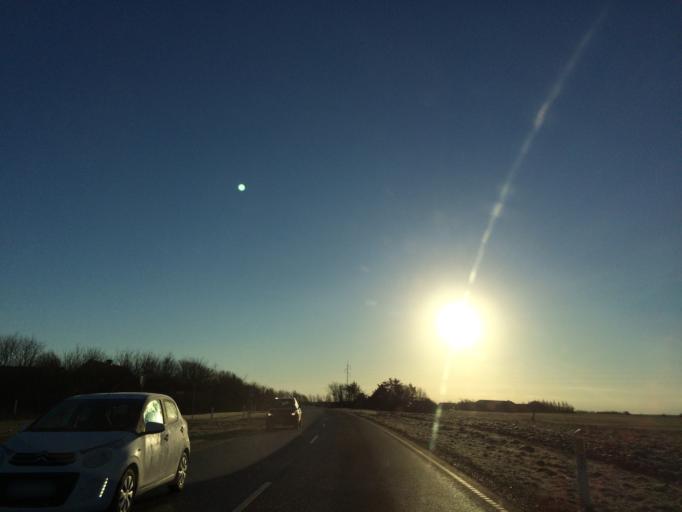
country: DK
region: Central Jutland
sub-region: Lemvig Kommune
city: Lemvig
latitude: 56.5300
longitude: 8.3709
